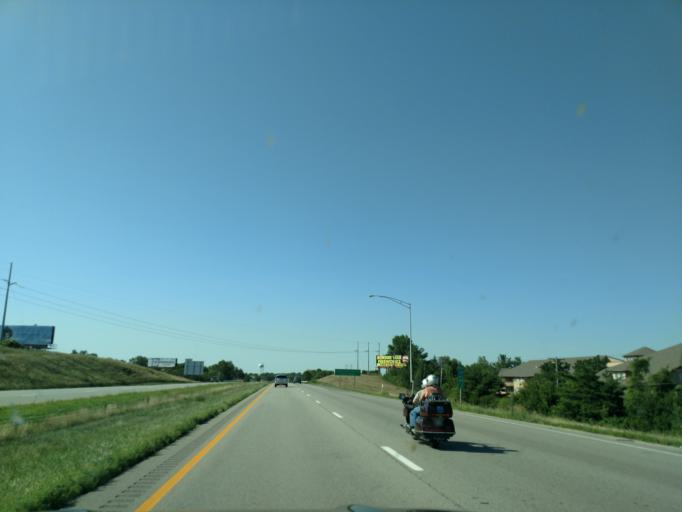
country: US
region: Missouri
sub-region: Buchanan County
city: Saint Joseph
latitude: 39.7801
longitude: -94.7941
